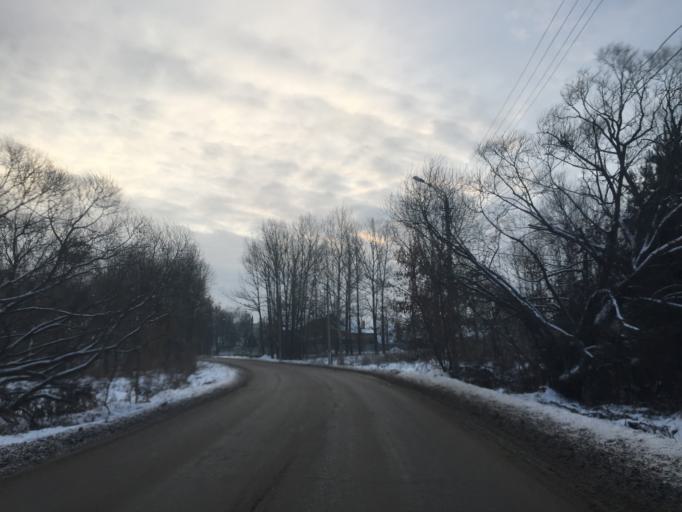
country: RU
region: Tula
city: Gorelki
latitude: 54.2360
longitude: 37.6435
